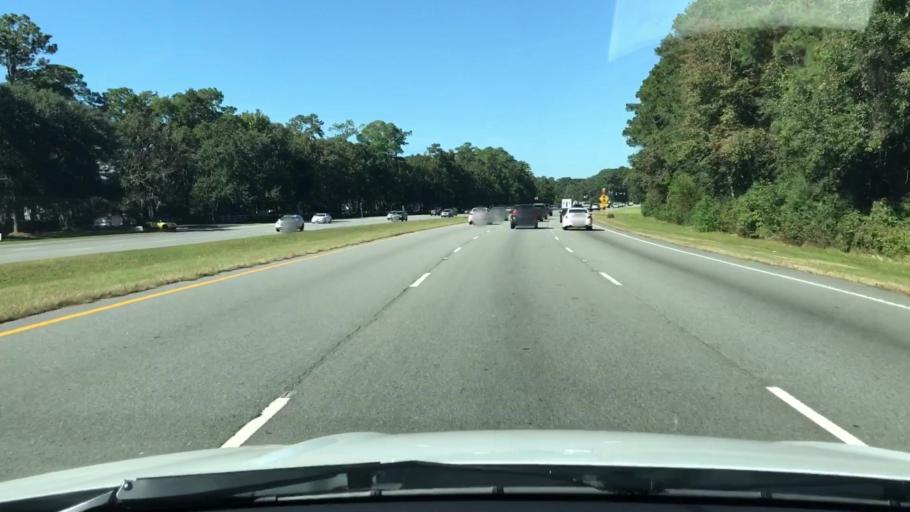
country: US
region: South Carolina
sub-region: Beaufort County
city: Bluffton
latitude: 32.2749
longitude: -80.8698
